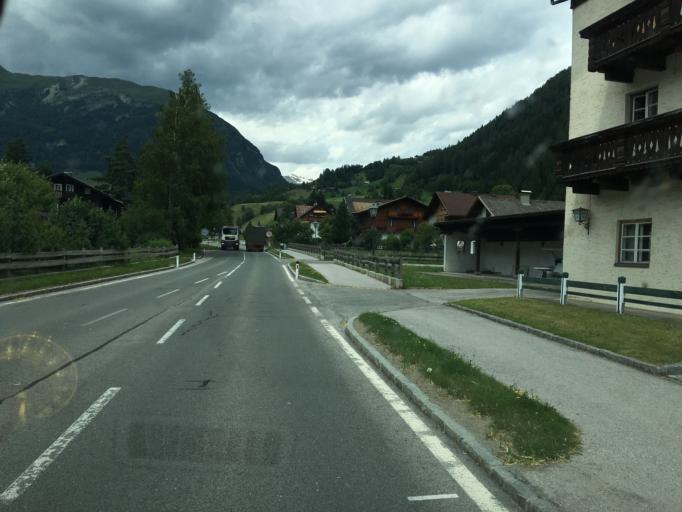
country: AT
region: Carinthia
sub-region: Politischer Bezirk Spittal an der Drau
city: Grosskirchheim
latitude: 46.9727
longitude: 12.8934
